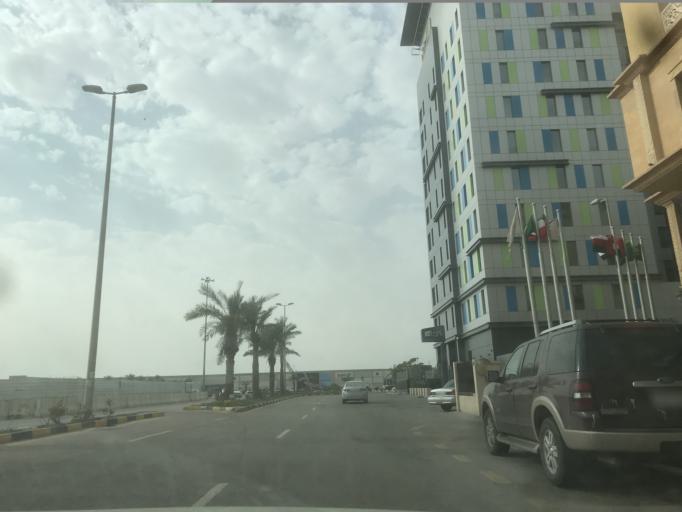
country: SA
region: Eastern Province
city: Khobar
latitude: 26.3040
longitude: 50.1747
